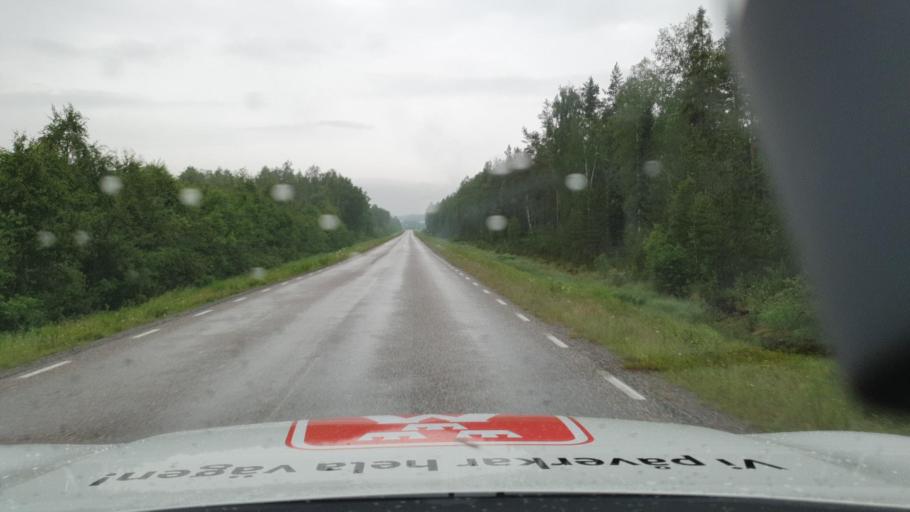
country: SE
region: Vaesterbotten
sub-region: Vannas Kommun
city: Vaennaes
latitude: 63.7822
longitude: 19.5892
